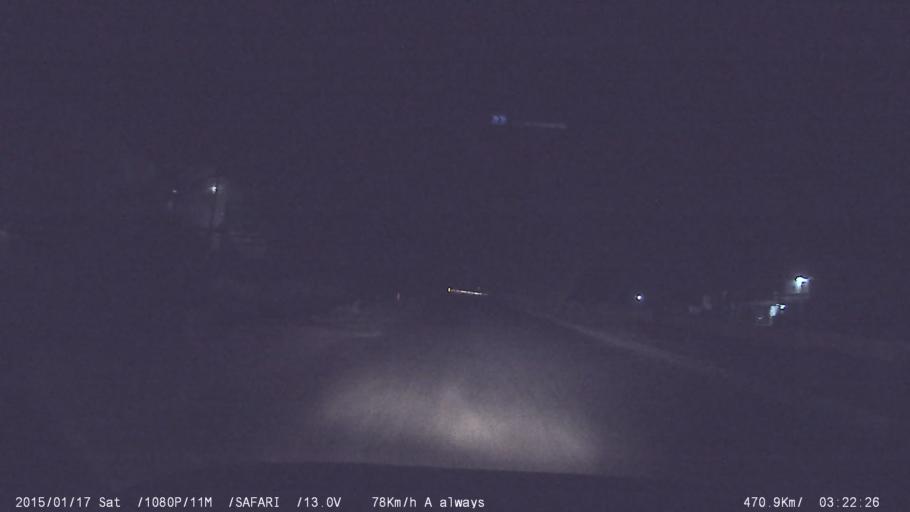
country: IN
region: Tamil Nadu
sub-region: Krishnagiri
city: Kelamangalam
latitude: 12.6621
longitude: 78.0118
